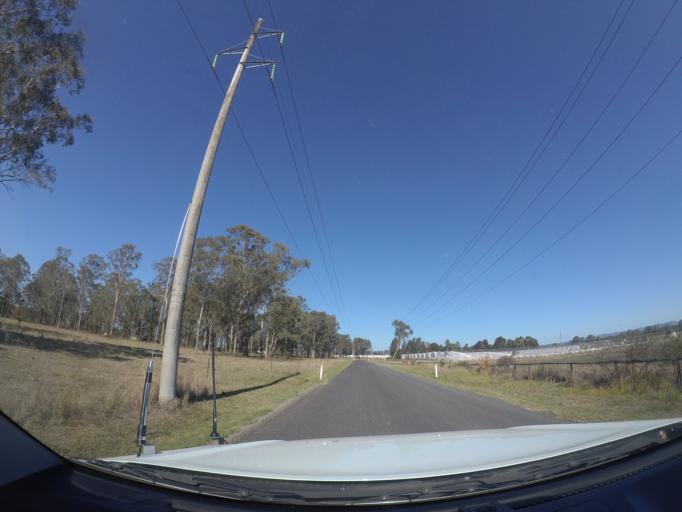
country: AU
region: Queensland
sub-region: Logan
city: Chambers Flat
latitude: -27.7602
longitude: 153.0760
